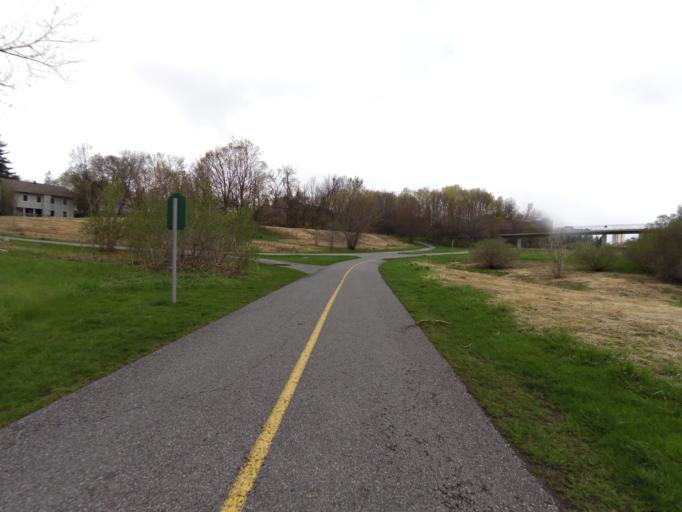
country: CA
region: Ontario
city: Bells Corners
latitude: 45.3613
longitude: -75.7826
